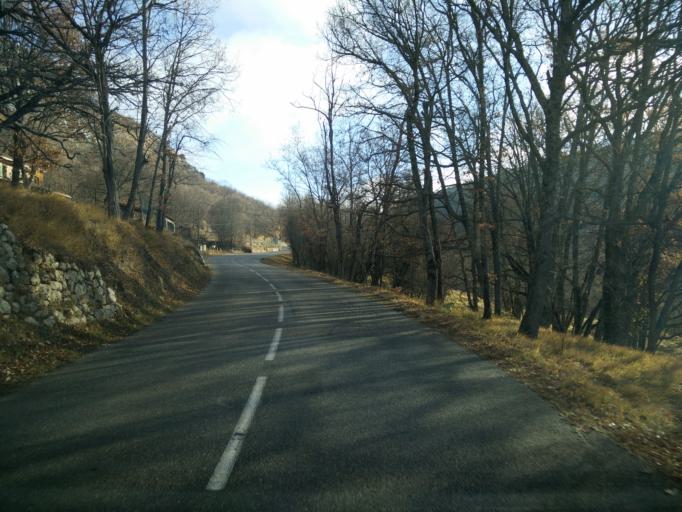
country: FR
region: Provence-Alpes-Cote d'Azur
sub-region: Departement des Alpes-Maritimes
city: Tourrettes-sur-Loup
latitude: 43.7863
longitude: 7.0153
